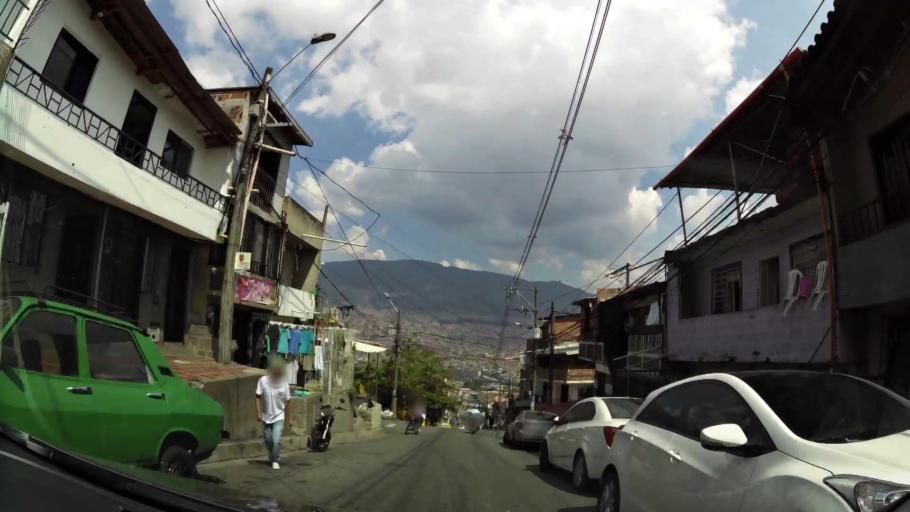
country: CO
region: Antioquia
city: Medellin
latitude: 6.2894
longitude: -75.5824
